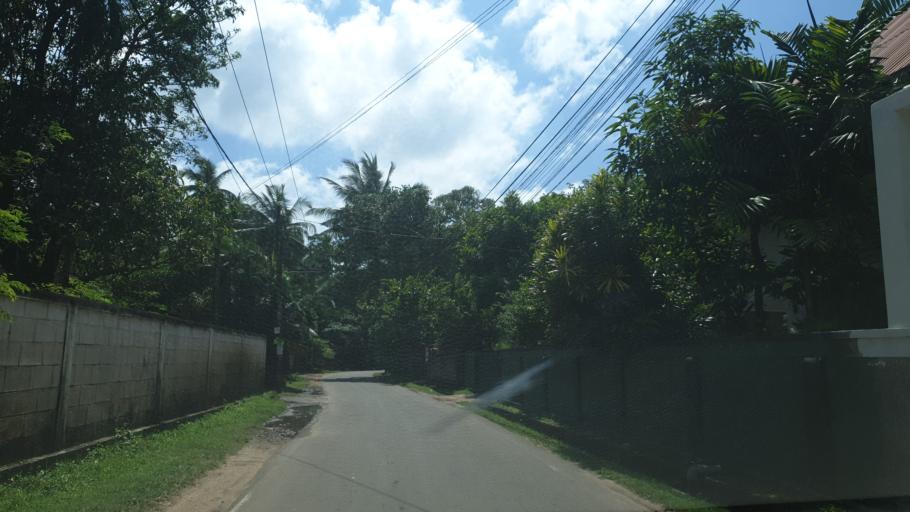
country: LK
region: Western
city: Panadura
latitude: 6.6852
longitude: 79.9303
